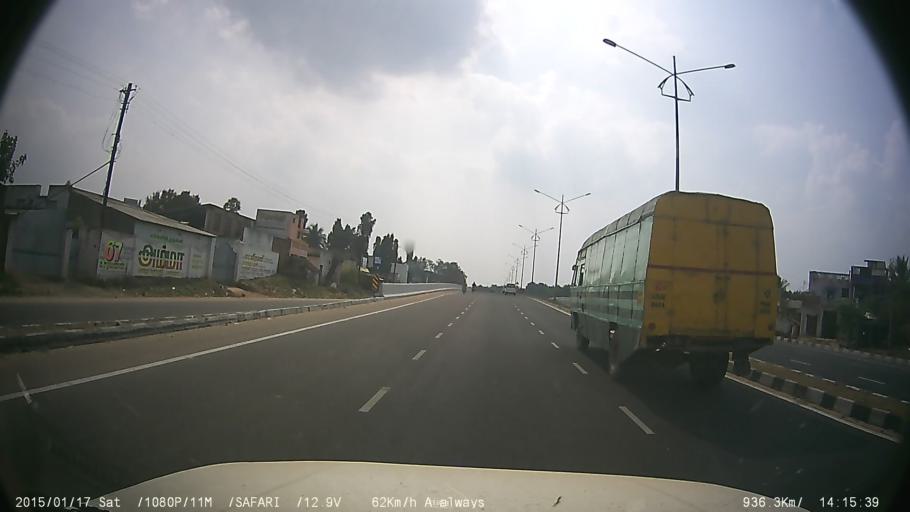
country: IN
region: Tamil Nadu
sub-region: Vellore
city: Ambur
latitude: 12.7639
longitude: 78.7048
